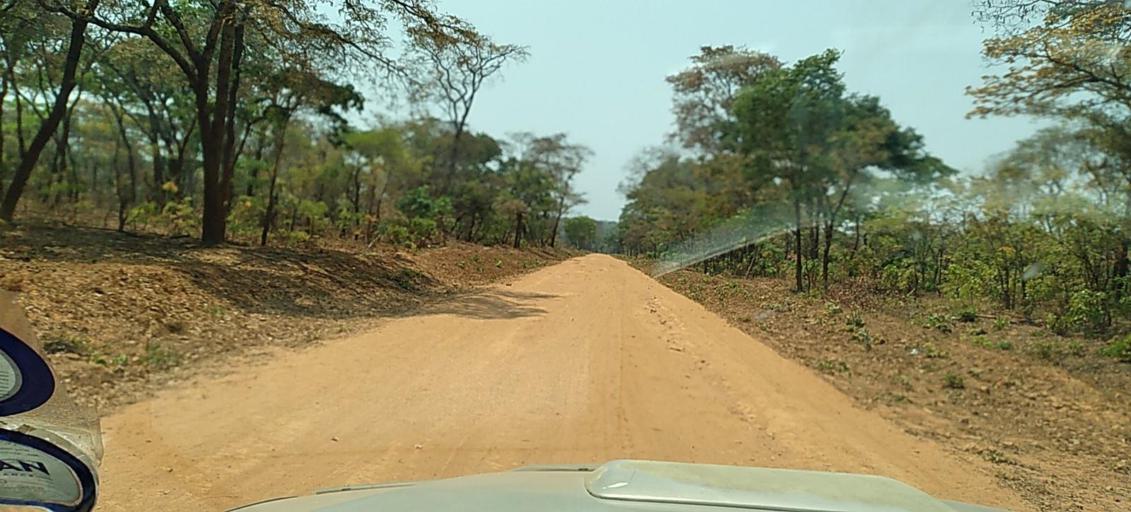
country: ZM
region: North-Western
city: Kasempa
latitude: -13.5466
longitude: 26.0367
